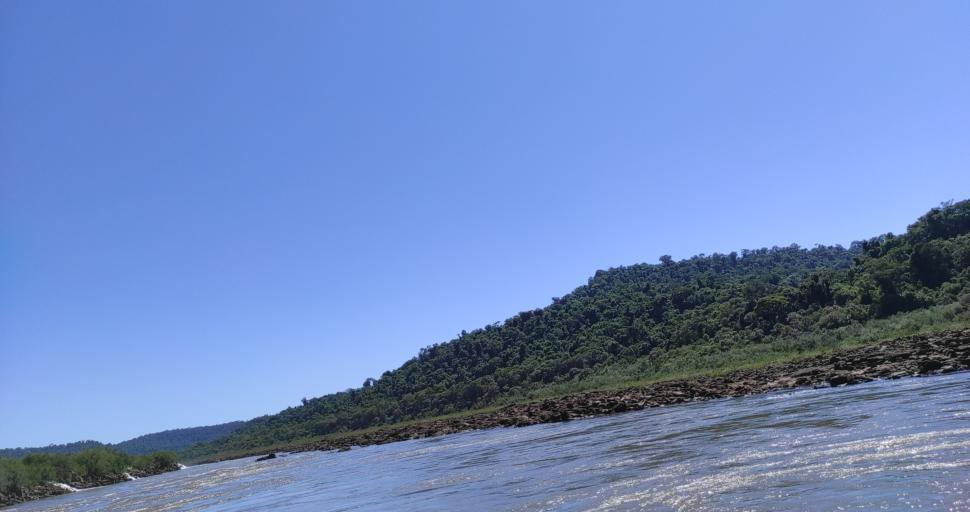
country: BR
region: Rio Grande do Sul
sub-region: Tres Passos
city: Tres Passos
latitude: -27.1549
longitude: -53.8893
